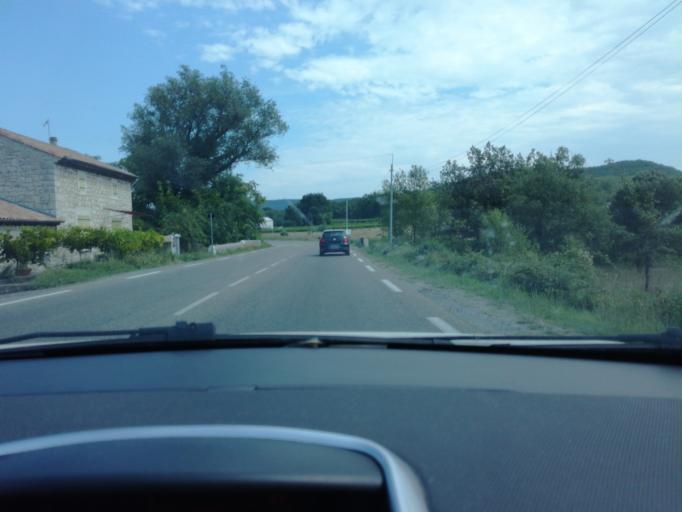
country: FR
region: Rhone-Alpes
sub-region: Departement de l'Ardeche
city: Ruoms
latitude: 44.4681
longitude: 4.3493
